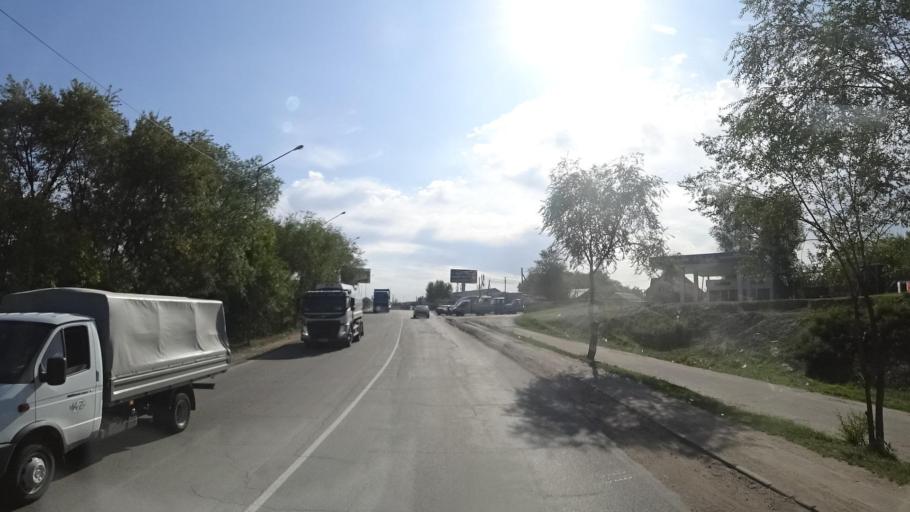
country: KZ
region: Almaty Oblysy
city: Energeticheskiy
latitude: 43.4066
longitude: 77.0134
